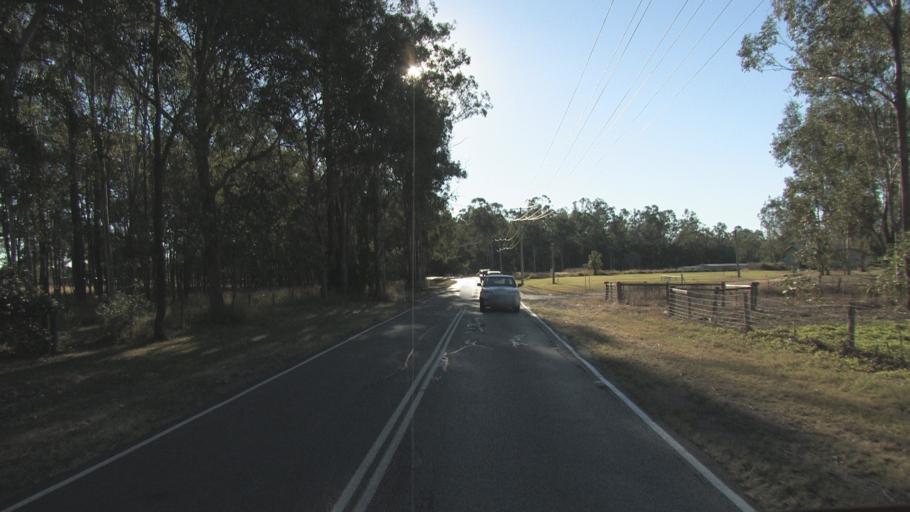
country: AU
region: Queensland
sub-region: Logan
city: Chambers Flat
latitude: -27.7478
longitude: 153.0749
